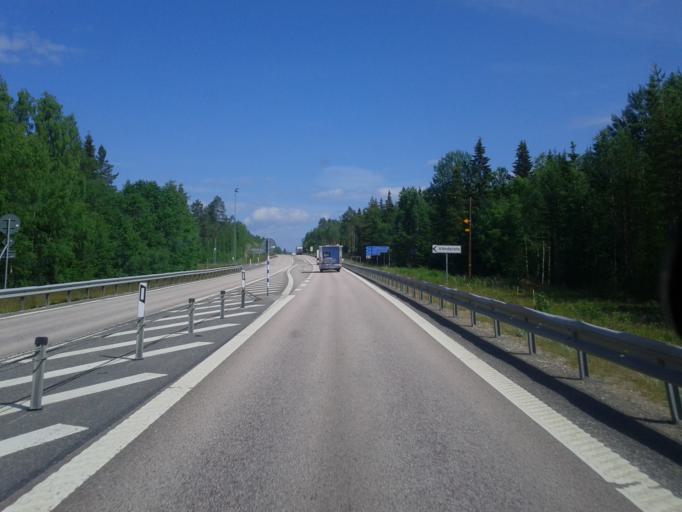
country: SE
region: Vaesternorrland
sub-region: OErnskoeldsviks Kommun
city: Husum
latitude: 63.4627
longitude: 19.2636
